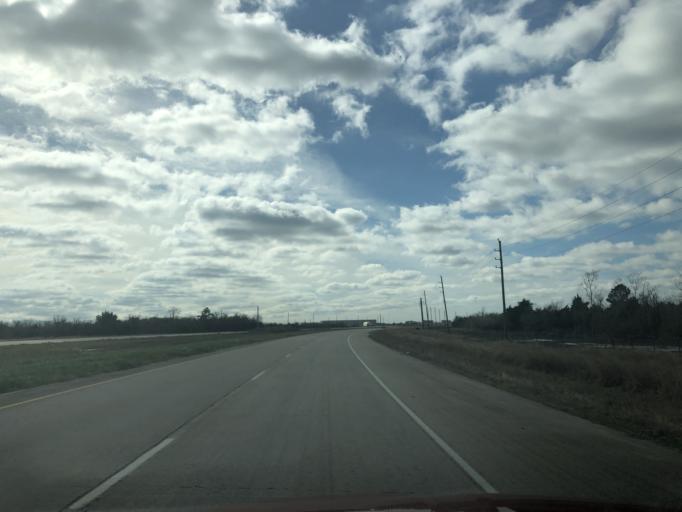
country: US
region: Texas
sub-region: Chambers County
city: Beach City
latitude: 29.7385
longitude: -94.8736
